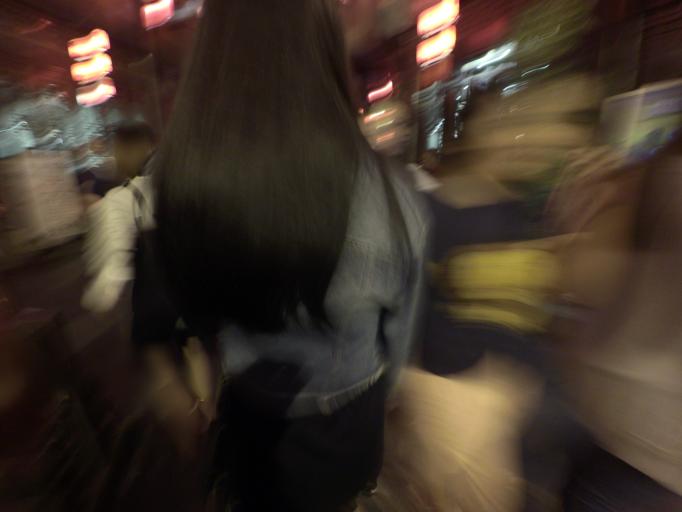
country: CN
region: Sichuan
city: Chengdu
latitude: 30.6472
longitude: 104.0474
